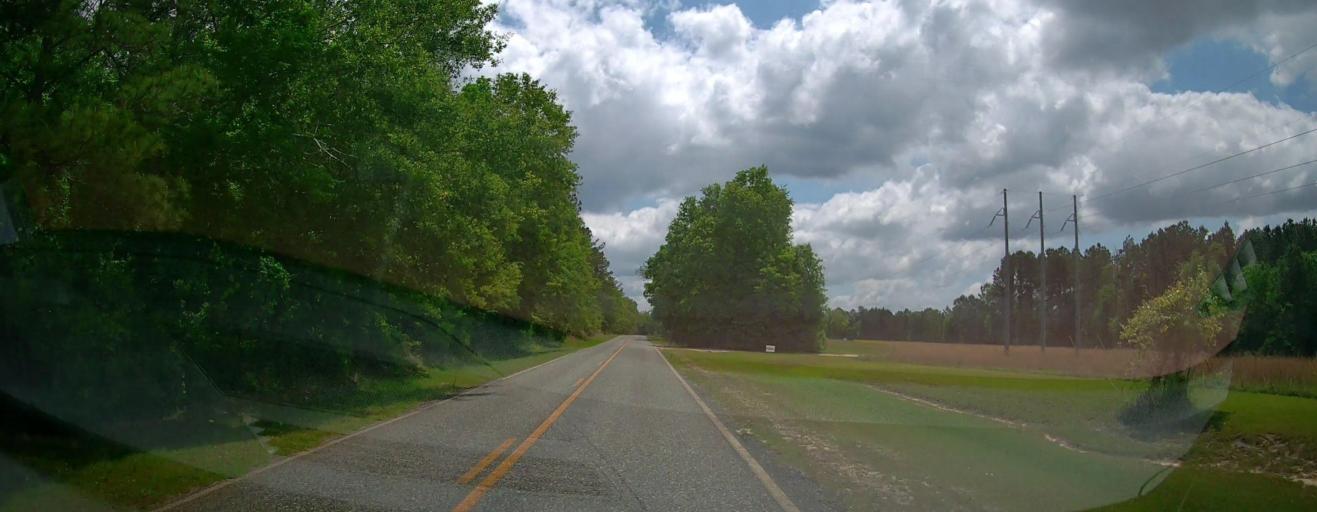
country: US
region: Georgia
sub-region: Laurens County
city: Dublin
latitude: 32.6075
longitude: -82.9402
